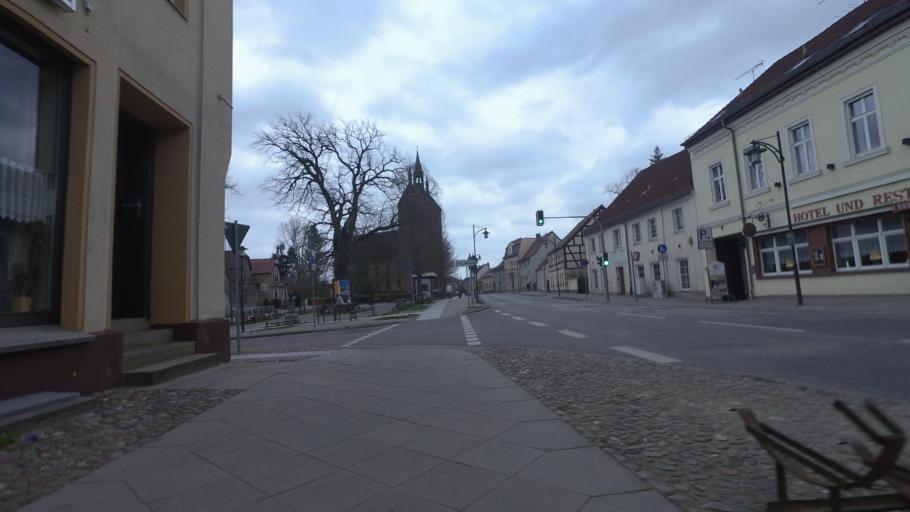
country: DE
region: Brandenburg
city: Neuruppin
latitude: 52.9504
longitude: 12.8426
